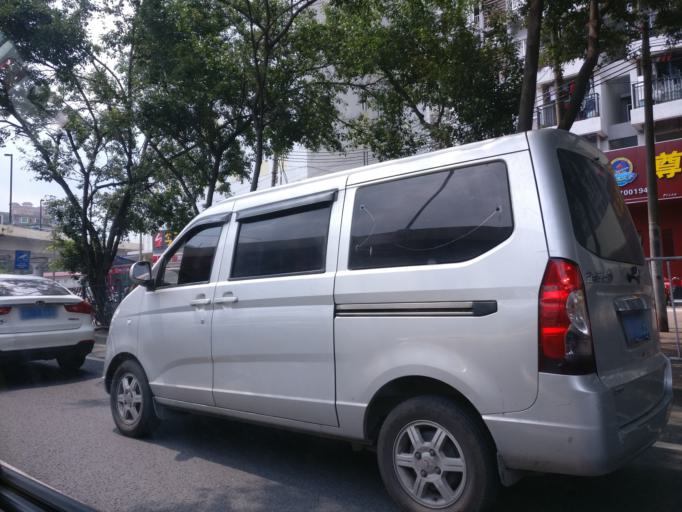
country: CN
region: Guangdong
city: Luopu
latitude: 23.0675
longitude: 113.2934
